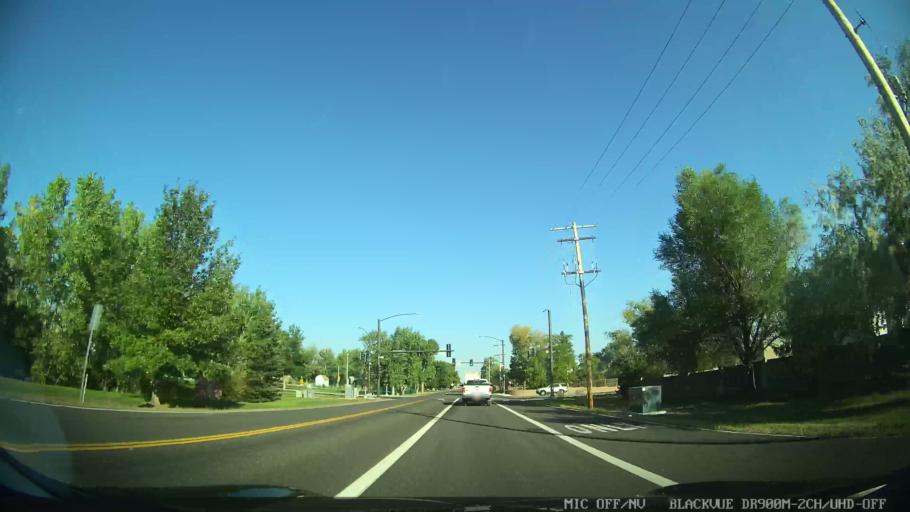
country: US
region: Colorado
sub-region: Larimer County
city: Loveland
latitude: 40.4510
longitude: -105.0694
